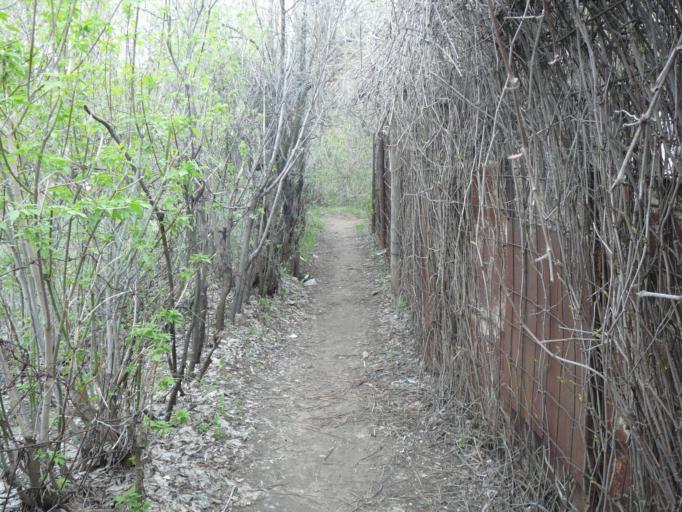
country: RU
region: Saratov
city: Engel's
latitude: 51.4607
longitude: 46.1729
